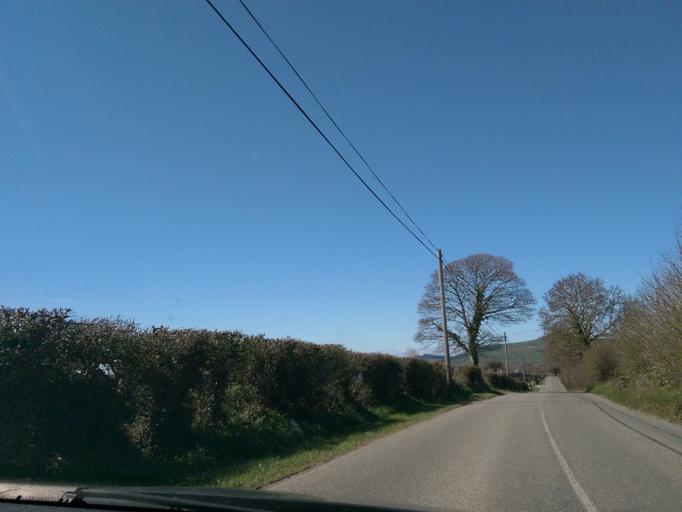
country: IE
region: Leinster
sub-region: Wicklow
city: Baltinglass
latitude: 52.9103
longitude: -6.6315
